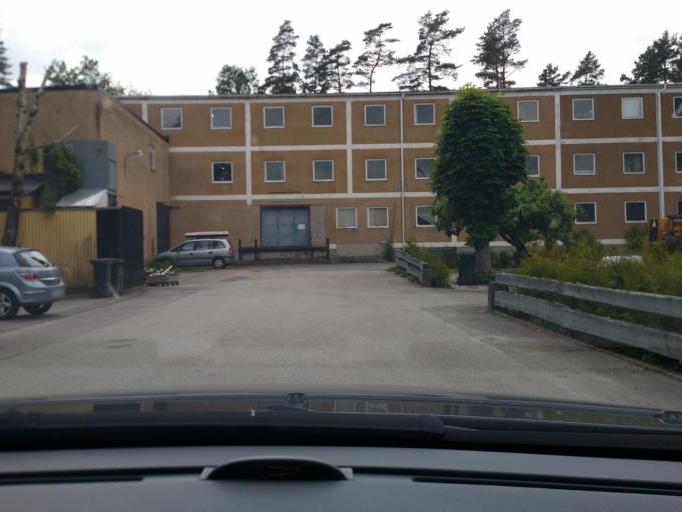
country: SE
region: Kronoberg
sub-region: Vaxjo Kommun
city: Lammhult
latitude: 57.1707
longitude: 14.5791
